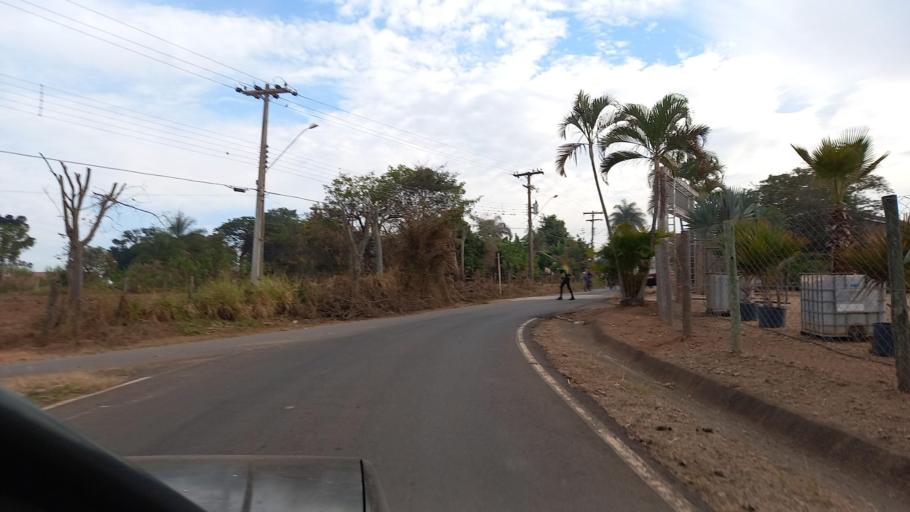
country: BR
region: Sao Paulo
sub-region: Moji-Guacu
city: Mogi-Gaucu
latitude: -22.3316
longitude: -46.8805
